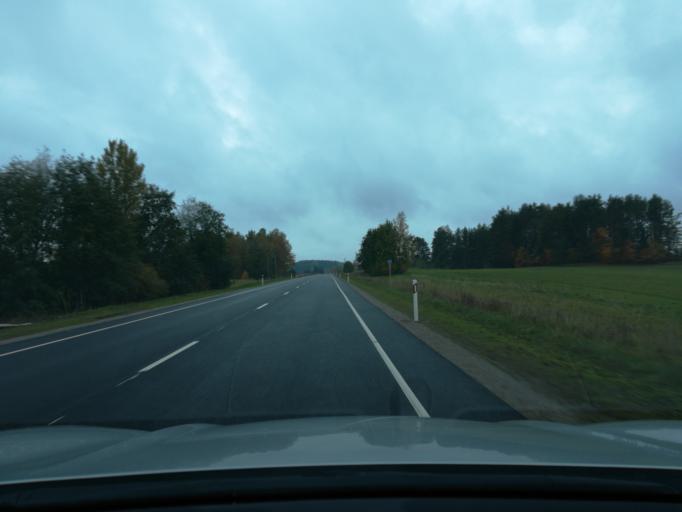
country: EE
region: Ida-Virumaa
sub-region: Johvi vald
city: Johvi
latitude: 59.1287
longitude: 27.3297
